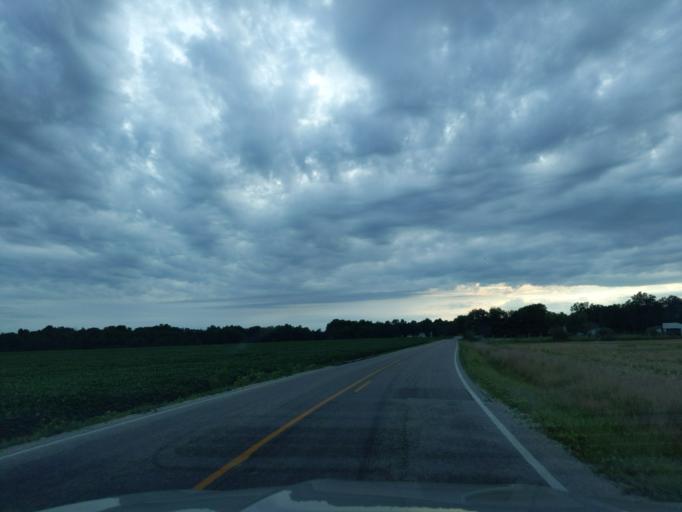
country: US
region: Indiana
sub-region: Ripley County
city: Sunman
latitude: 39.2020
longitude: -85.1741
